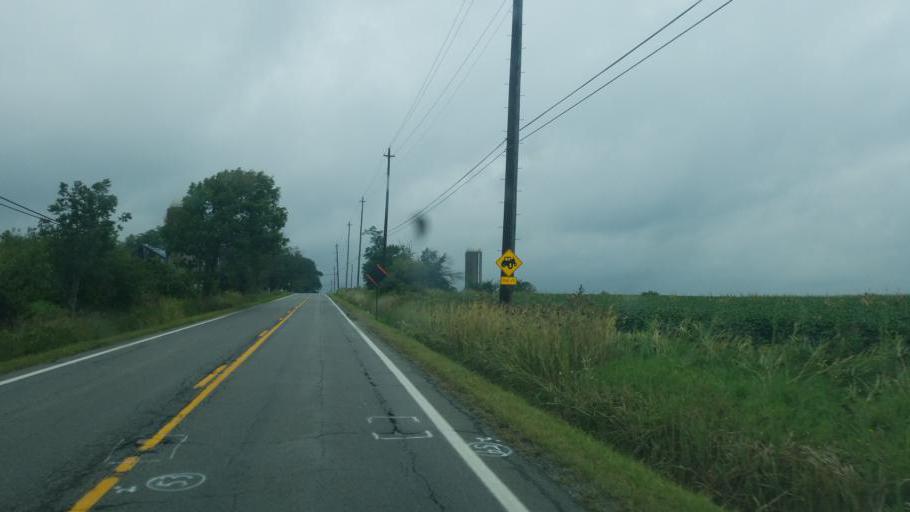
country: US
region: Ohio
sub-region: Geauga County
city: Burton
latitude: 41.4141
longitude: -81.2120
